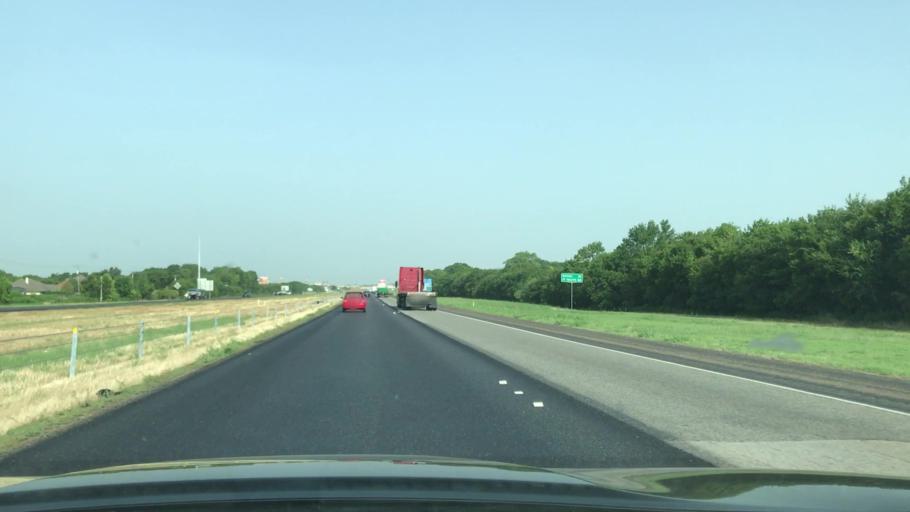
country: US
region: Texas
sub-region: Kaufman County
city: Terrell
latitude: 32.6964
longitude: -96.2564
